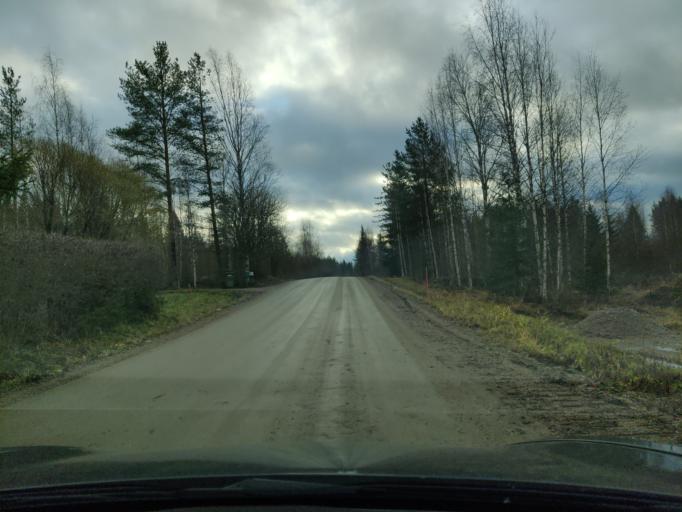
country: FI
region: Northern Savo
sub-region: Ylae-Savo
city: Kiuruvesi
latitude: 63.6398
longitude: 26.6332
